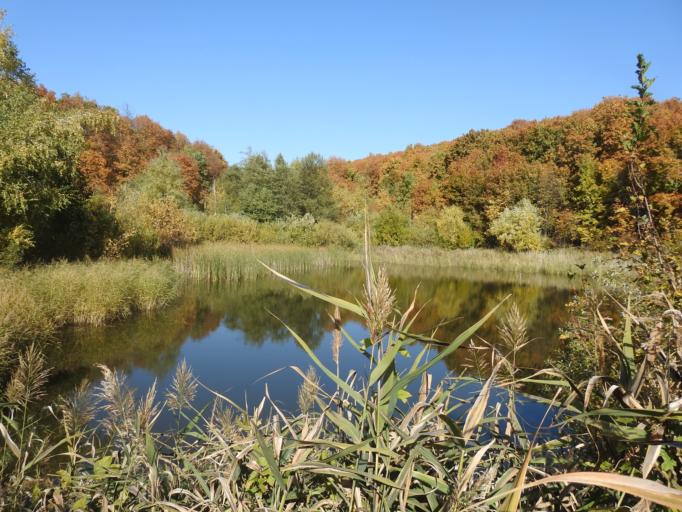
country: RU
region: Saratov
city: Baltay
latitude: 52.4837
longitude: 46.7230
